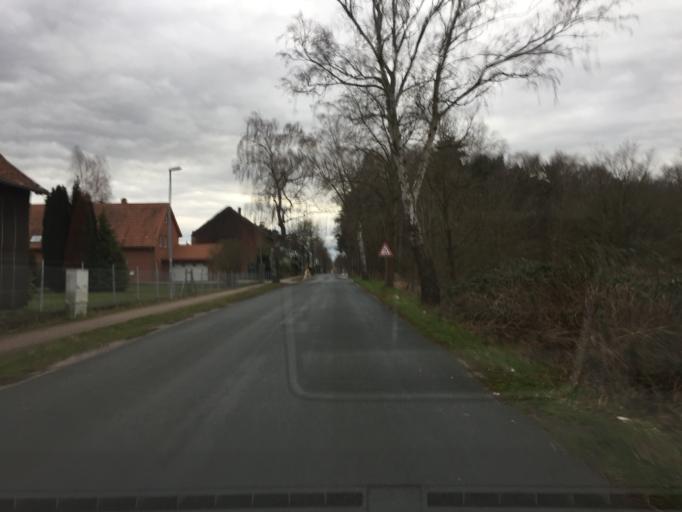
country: DE
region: Lower Saxony
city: Neustadt am Rubenberge
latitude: 52.4736
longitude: 9.4904
